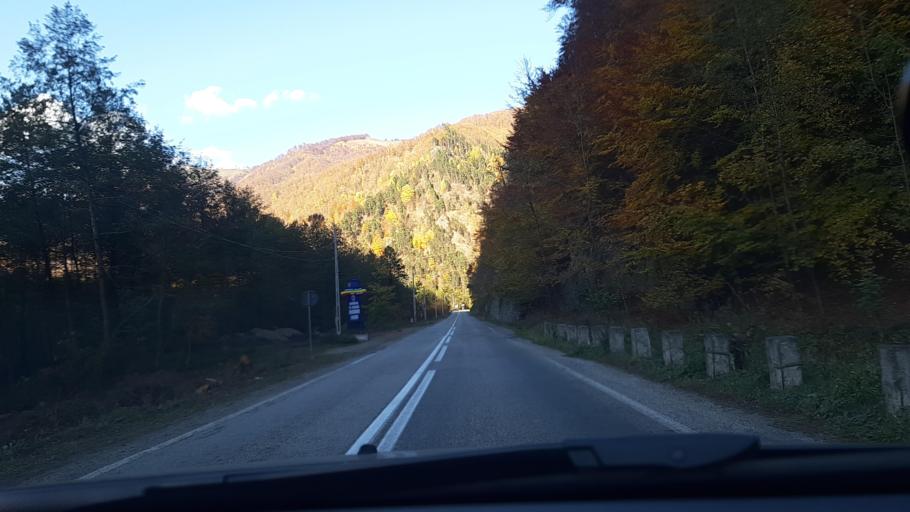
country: RO
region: Valcea
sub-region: Comuna Brezoi
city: Brezoi
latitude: 45.3482
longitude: 24.1511
